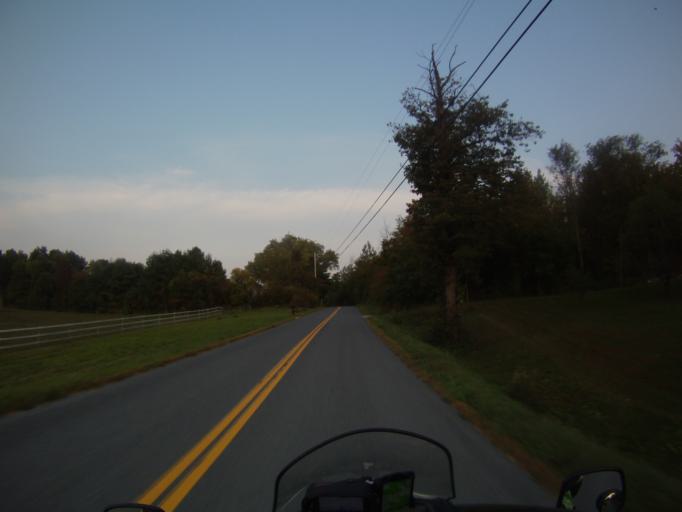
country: US
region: Vermont
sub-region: Rutland County
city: Brandon
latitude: 43.7928
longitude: -73.1030
